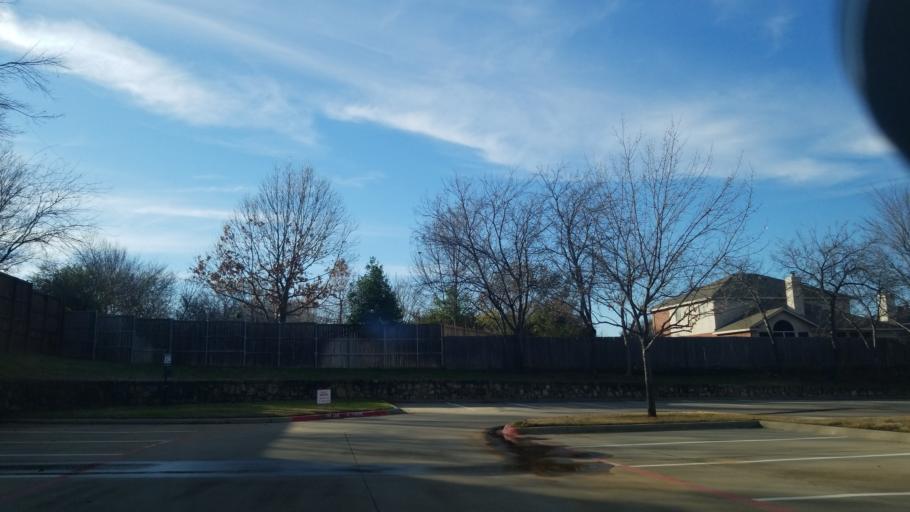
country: US
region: Texas
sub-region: Denton County
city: Corinth
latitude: 33.1398
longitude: -97.0575
